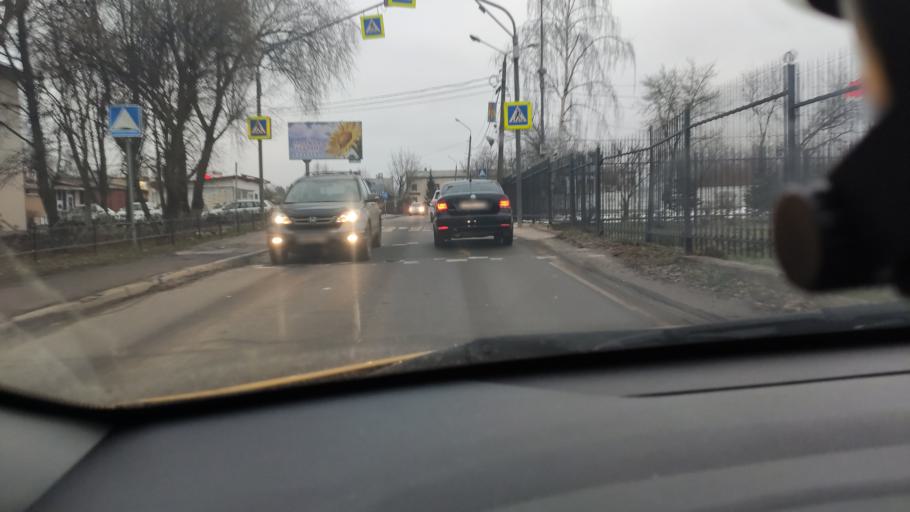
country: RU
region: Moskovskaya
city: Biryulevo Zapadnoye
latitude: 55.5625
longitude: 37.6448
